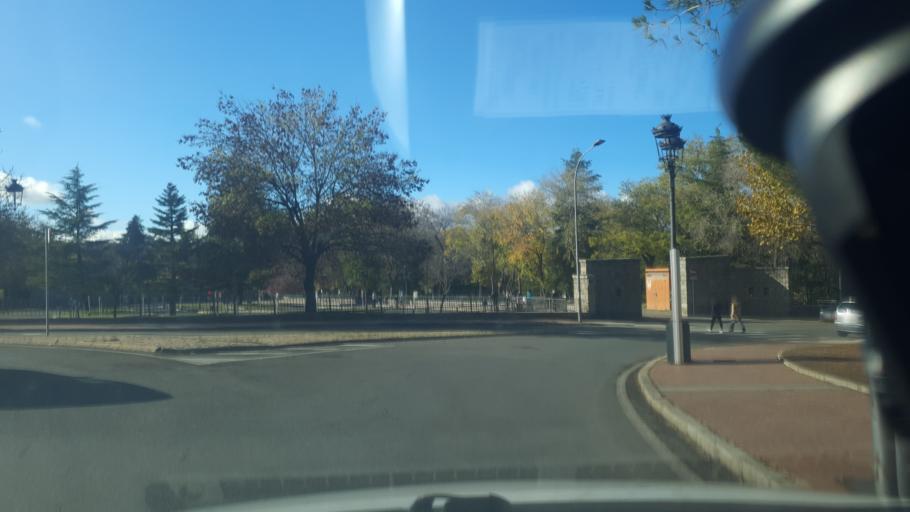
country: ES
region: Castille and Leon
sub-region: Provincia de Avila
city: Avila
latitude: 40.6583
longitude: -4.6844
